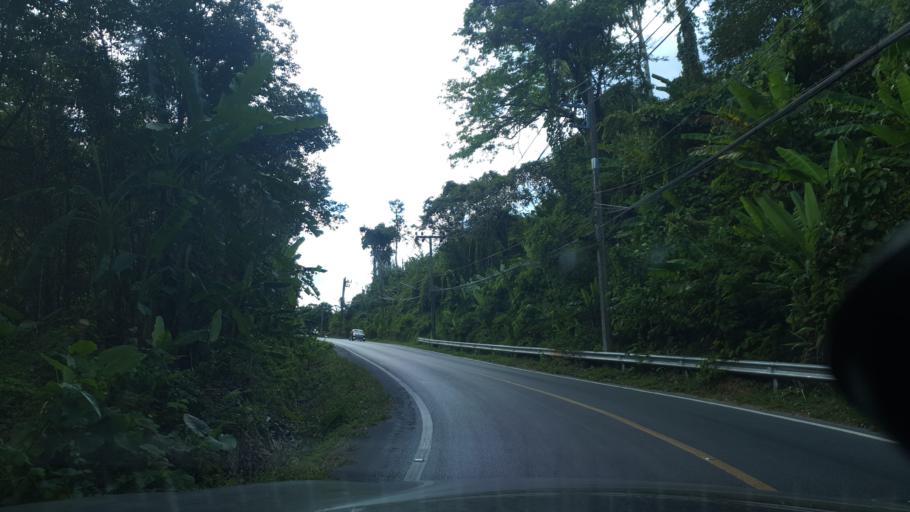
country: TH
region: Phuket
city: Thalang
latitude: 8.0648
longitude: 98.2881
